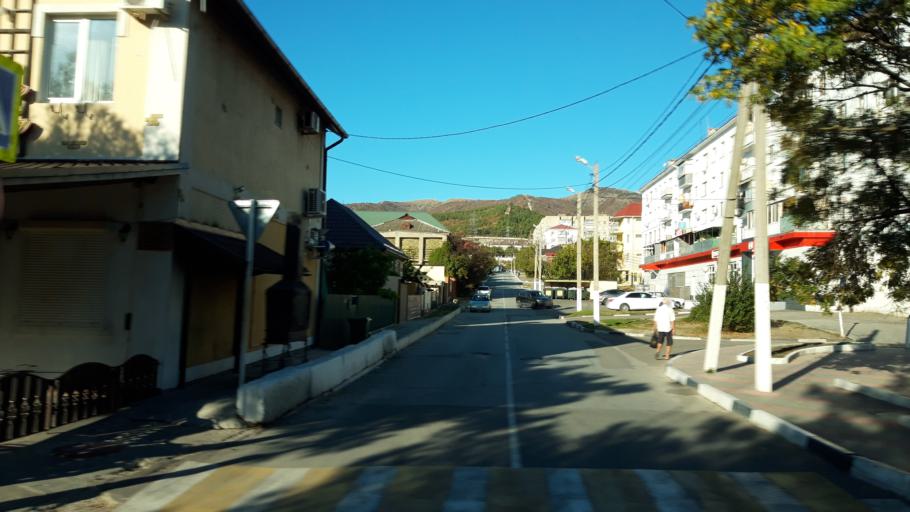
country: RU
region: Krasnodarskiy
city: Kabardinka
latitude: 44.6509
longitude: 37.9415
